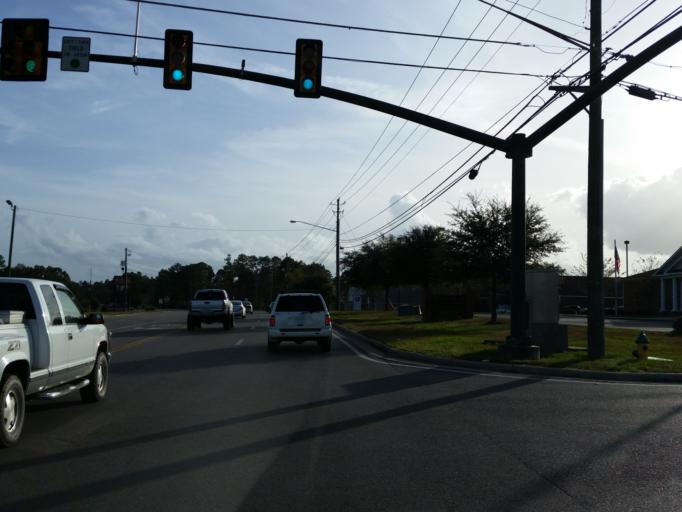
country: US
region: Mississippi
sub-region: Forrest County
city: Hattiesburg
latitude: 31.2992
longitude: -89.3240
